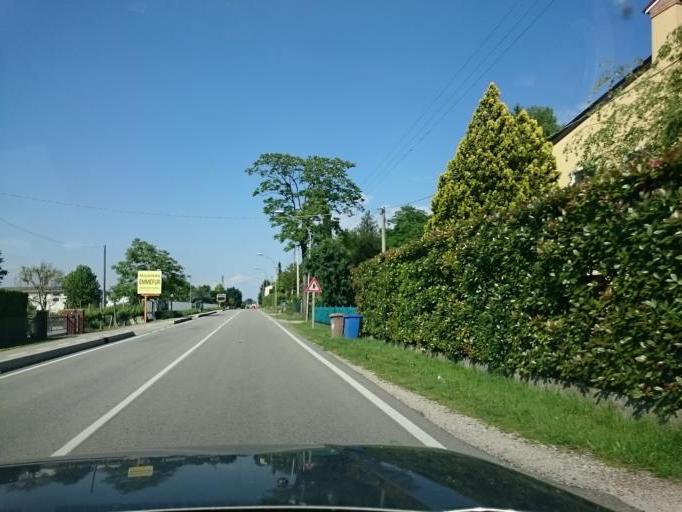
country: IT
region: Veneto
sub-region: Provincia di Vicenza
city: Montegalda
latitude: 45.4547
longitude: 11.6870
